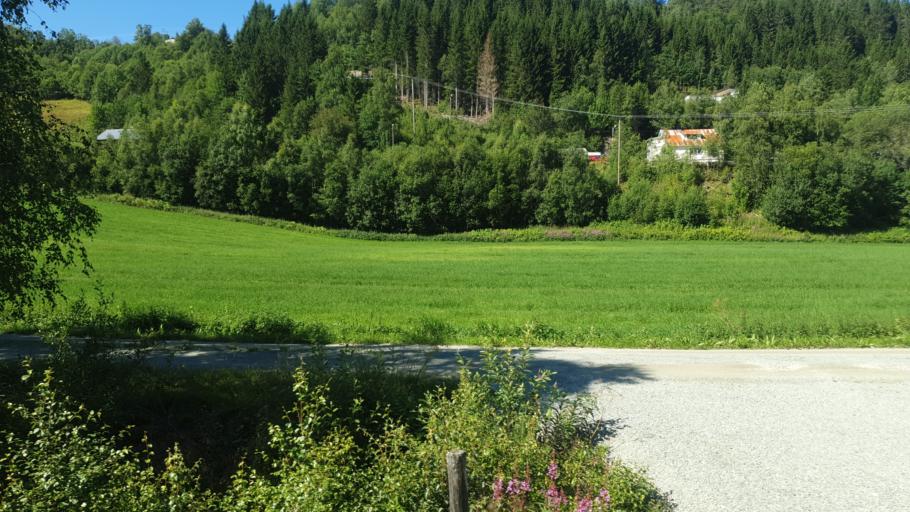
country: NO
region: Sor-Trondelag
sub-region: Meldal
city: Meldal
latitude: 63.1320
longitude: 9.7089
